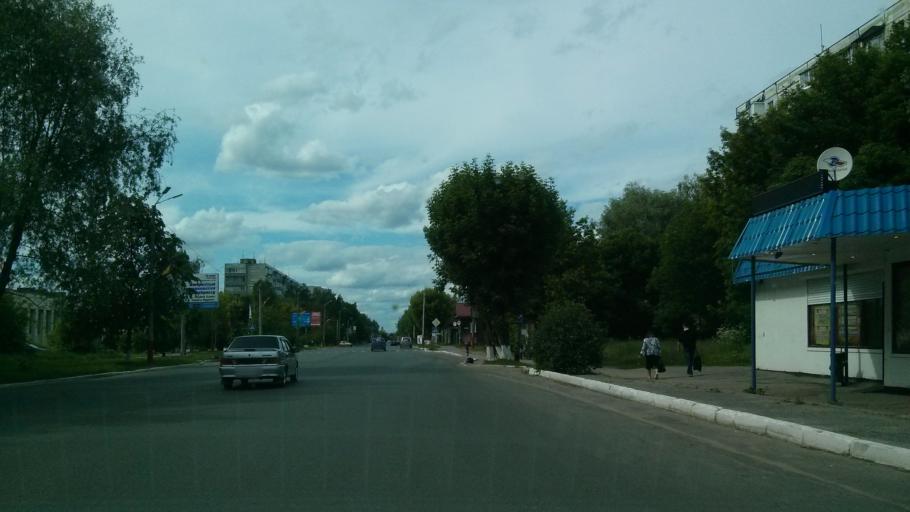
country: RU
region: Vladimir
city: Murom
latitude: 55.5683
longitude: 42.0604
